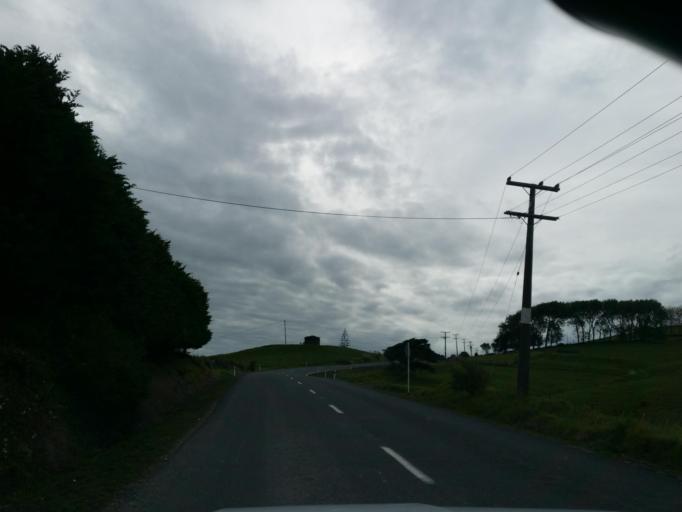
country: NZ
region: Northland
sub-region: Kaipara District
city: Dargaville
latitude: -35.9652
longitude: 173.9315
